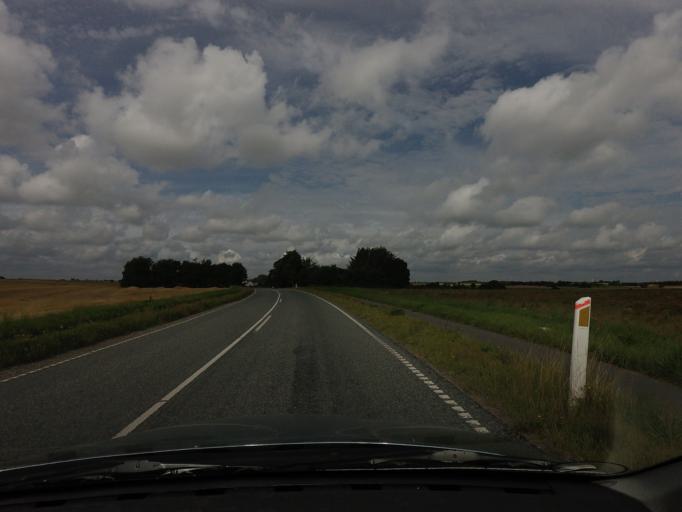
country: DK
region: North Denmark
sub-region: Hjorring Kommune
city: Sindal
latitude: 57.3421
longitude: 10.2926
